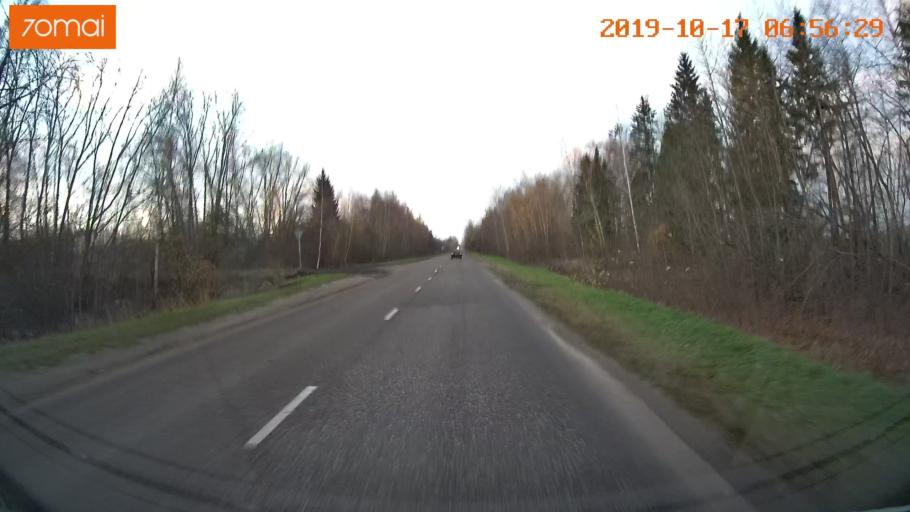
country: RU
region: Vladimir
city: Suzdal'
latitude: 56.4460
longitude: 40.4473
